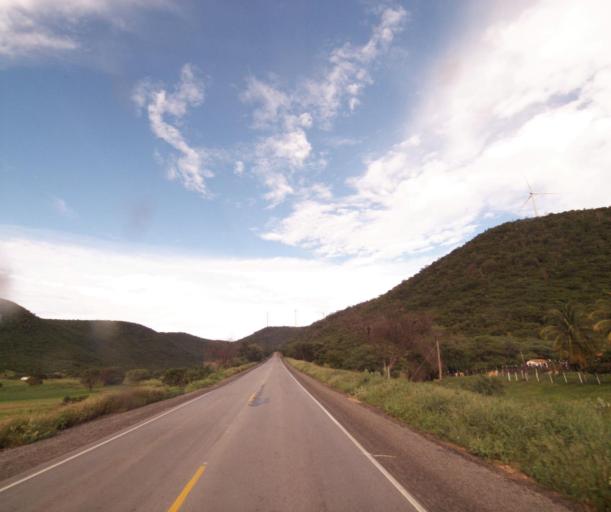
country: BR
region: Bahia
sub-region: Guanambi
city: Guanambi
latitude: -14.1563
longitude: -42.7057
